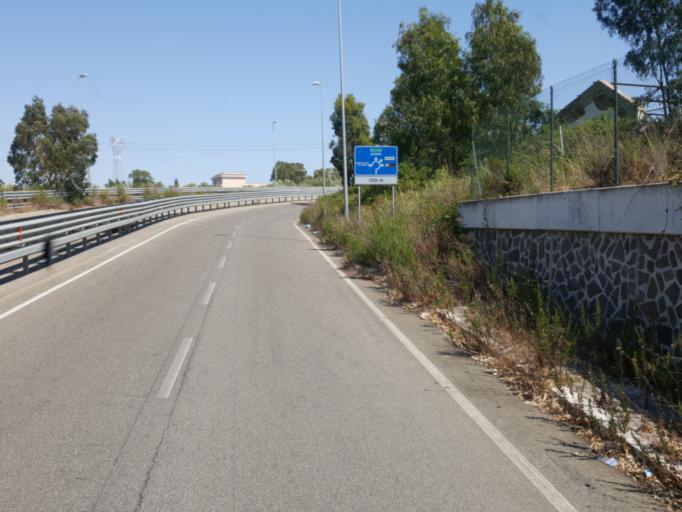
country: IT
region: Latium
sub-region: Citta metropolitana di Roma Capitale
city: Aurelia
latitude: 42.1288
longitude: 11.7865
